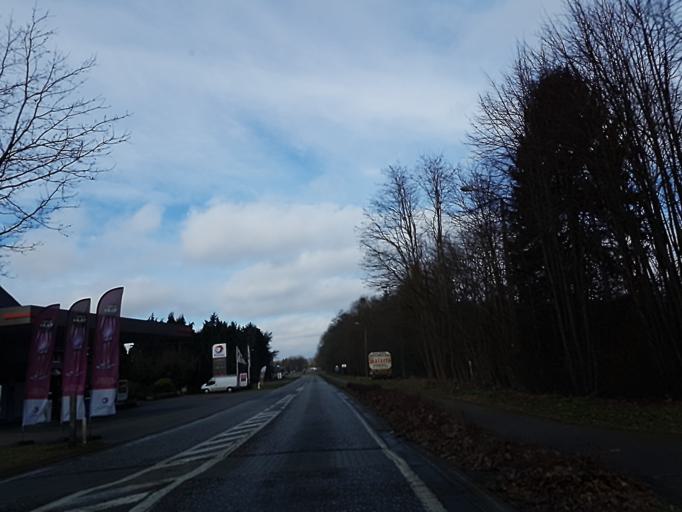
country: BE
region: Flanders
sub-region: Provincie Antwerpen
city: Westerlo
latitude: 51.0769
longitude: 4.9161
